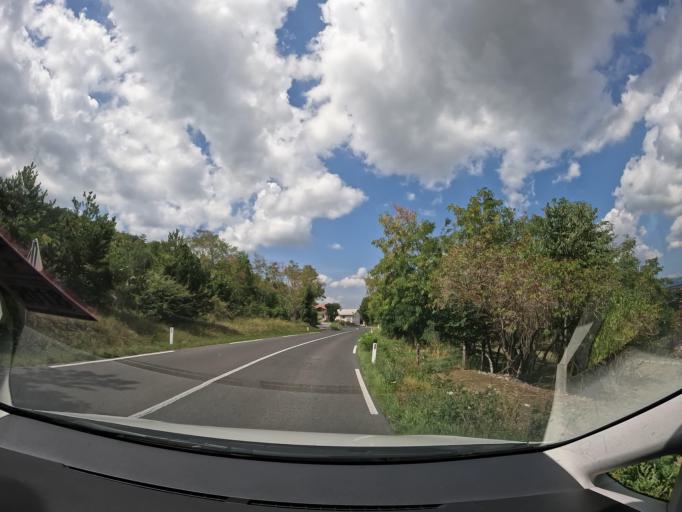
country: SI
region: Ilirska Bistrica
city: Ilirska Bistrica
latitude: 45.6201
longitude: 14.2493
